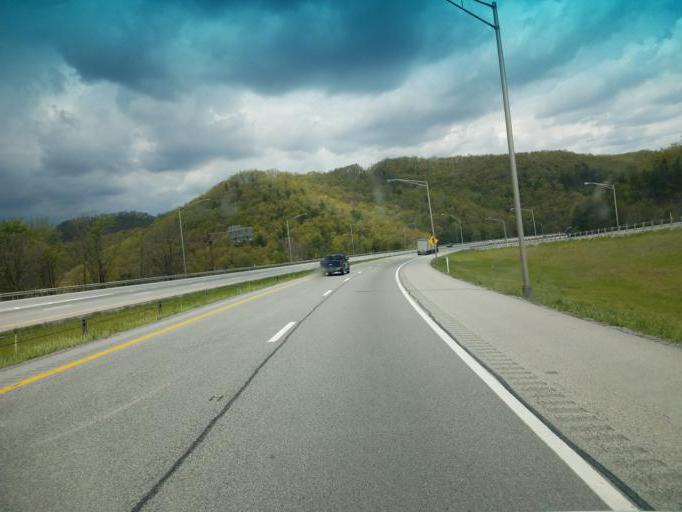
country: US
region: West Virginia
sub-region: Mercer County
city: Princeton
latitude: 37.2879
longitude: -81.1257
